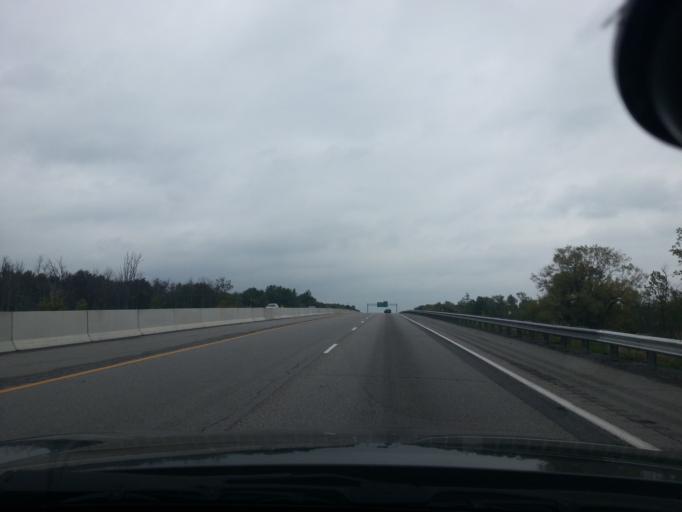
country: CA
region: Ontario
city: Prescott
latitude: 44.7340
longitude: -75.5086
